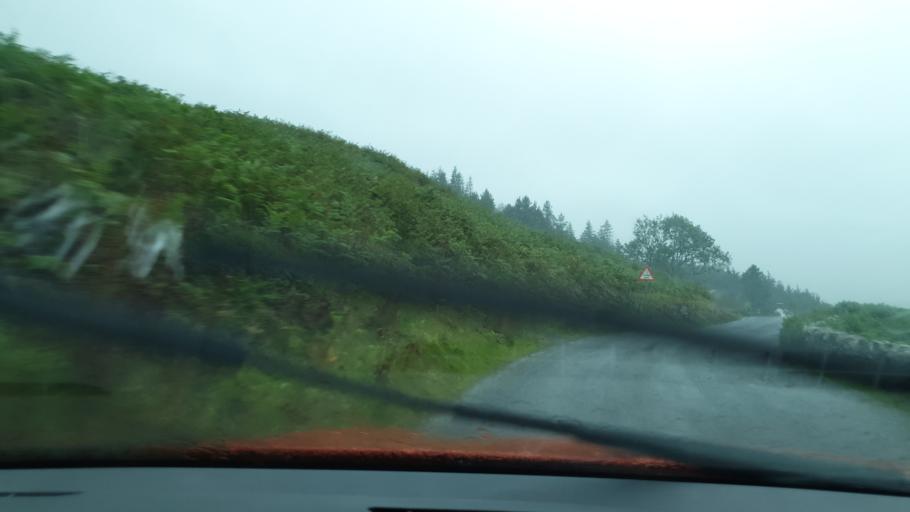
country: GB
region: England
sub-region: Cumbria
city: Millom
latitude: 54.3044
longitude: -3.2282
